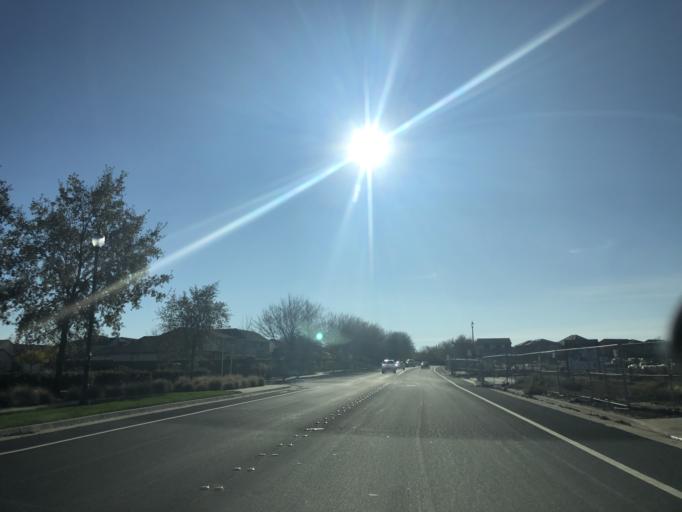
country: US
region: California
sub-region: Sacramento County
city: Antelope
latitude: 38.7850
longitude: -121.3687
